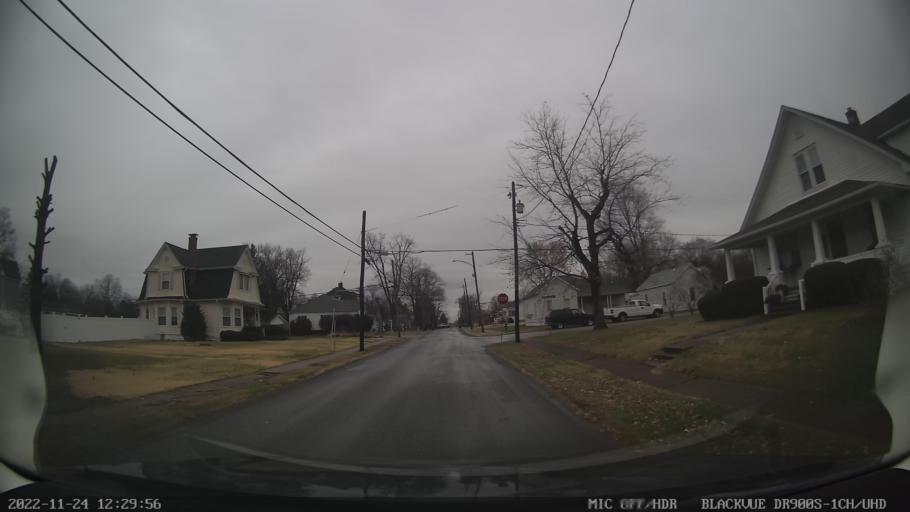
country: US
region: Illinois
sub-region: Macoupin County
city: Staunton
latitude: 39.0155
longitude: -89.7874
